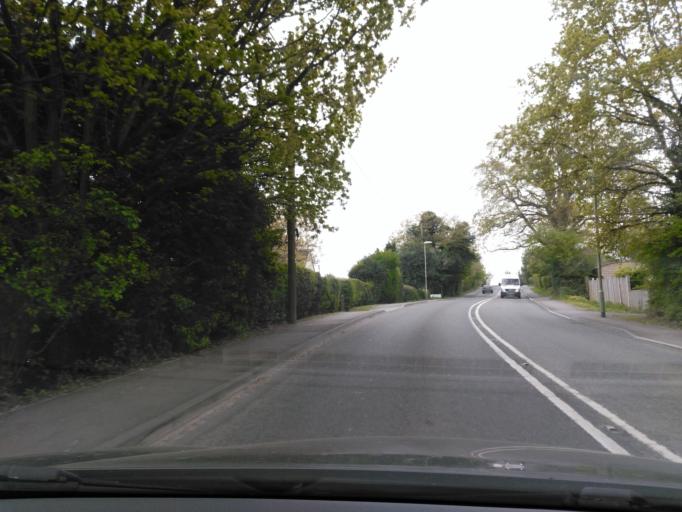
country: GB
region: England
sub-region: Hampshire
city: Tadley
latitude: 51.3473
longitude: -1.1341
